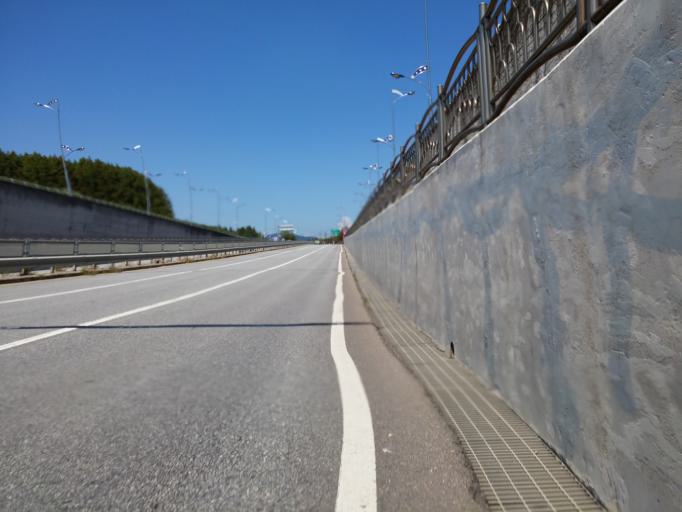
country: KR
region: Chungcheongbuk-do
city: Cheongju-si
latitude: 36.6254
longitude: 127.3375
